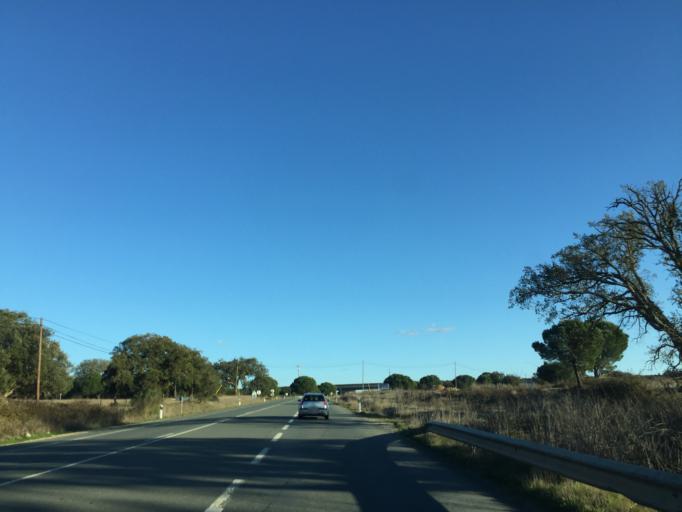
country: PT
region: Setubal
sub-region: Grandola
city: Grandola
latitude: 38.1190
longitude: -8.4237
